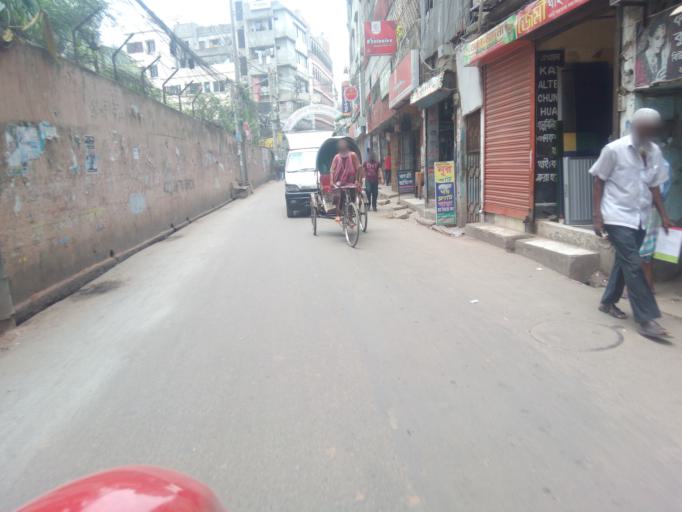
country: BD
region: Dhaka
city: Azimpur
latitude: 23.7194
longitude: 90.3900
